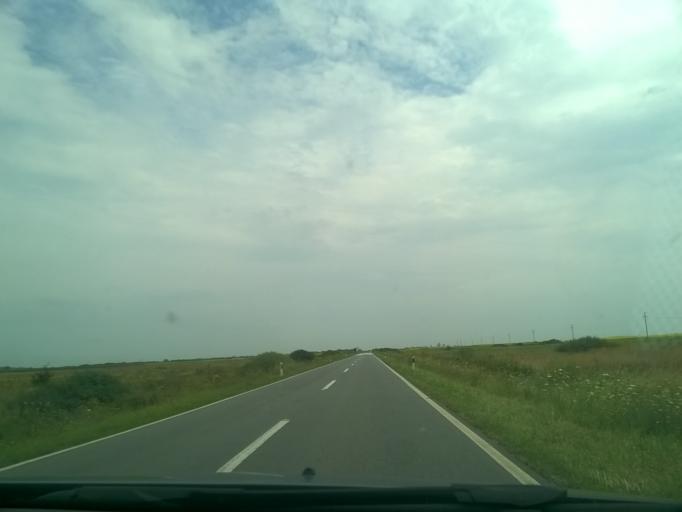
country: RS
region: Autonomna Pokrajina Vojvodina
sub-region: Srednjebanatski Okrug
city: Secanj
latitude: 45.3490
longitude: 20.7889
